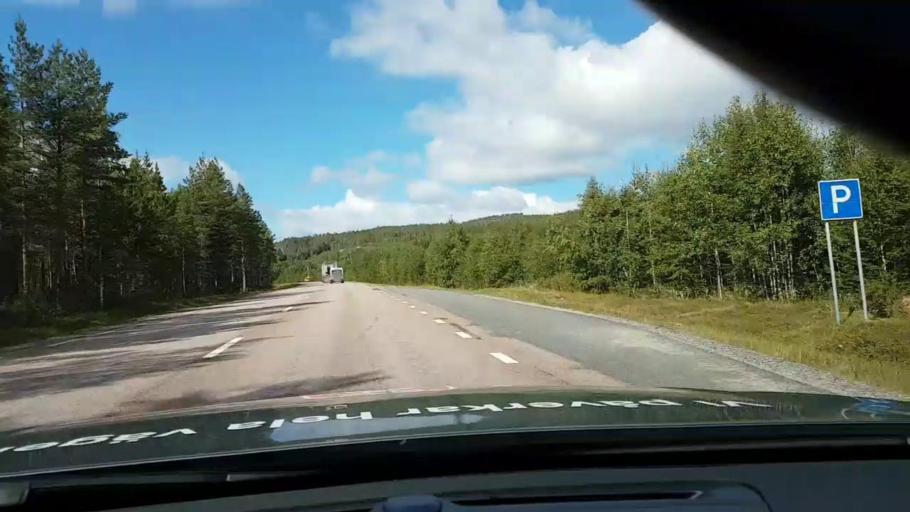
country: SE
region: Vaesternorrland
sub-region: OErnskoeldsviks Kommun
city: Bjasta
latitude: 63.3781
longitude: 18.4220
